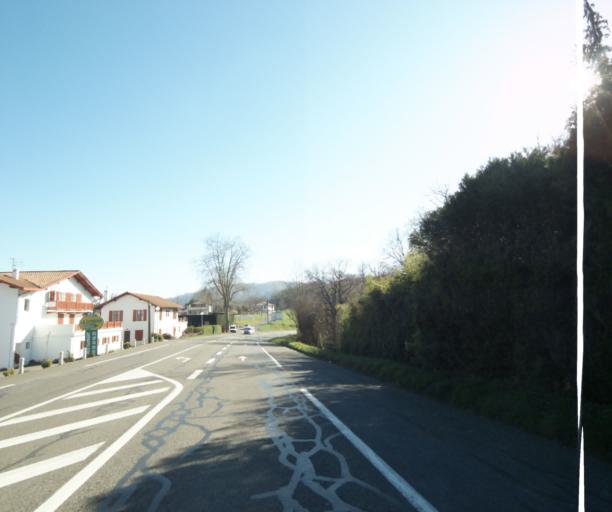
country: FR
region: Aquitaine
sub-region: Departement des Pyrenees-Atlantiques
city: Hendaye
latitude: 43.3485
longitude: -1.7489
